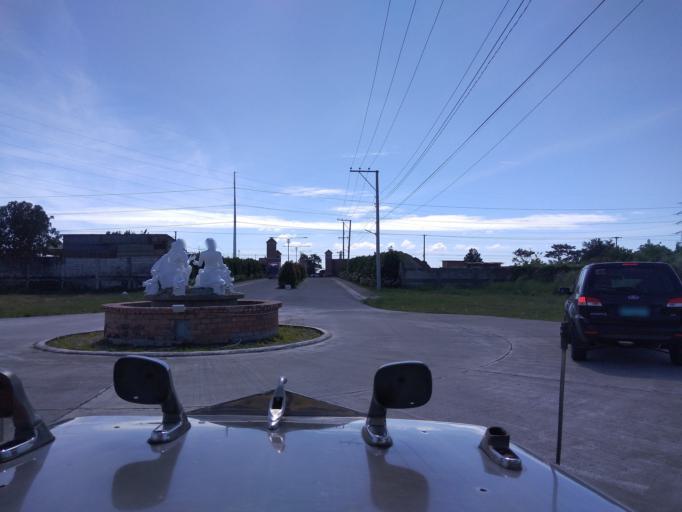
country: PH
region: Central Luzon
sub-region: Province of Pampanga
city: San Juan
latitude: 15.0187
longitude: 120.6638
